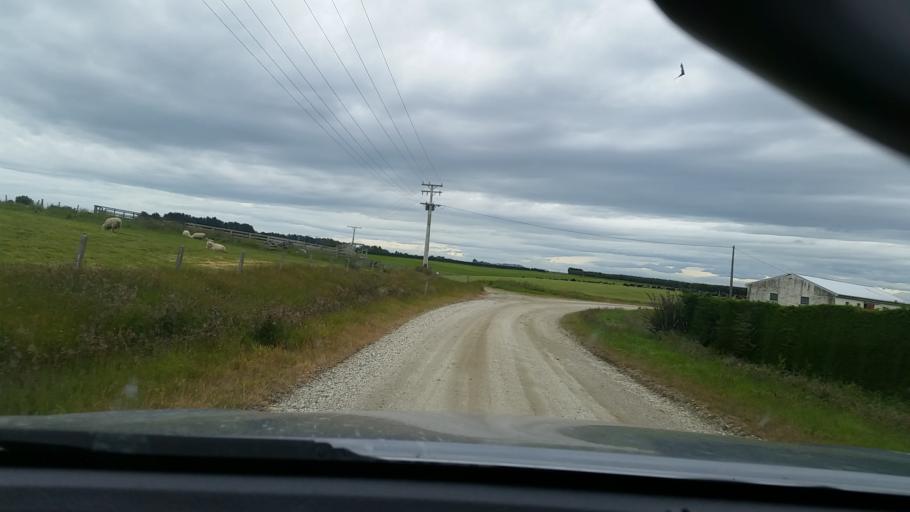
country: NZ
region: Southland
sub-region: Gore District
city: Gore
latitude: -46.2768
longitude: 168.7231
